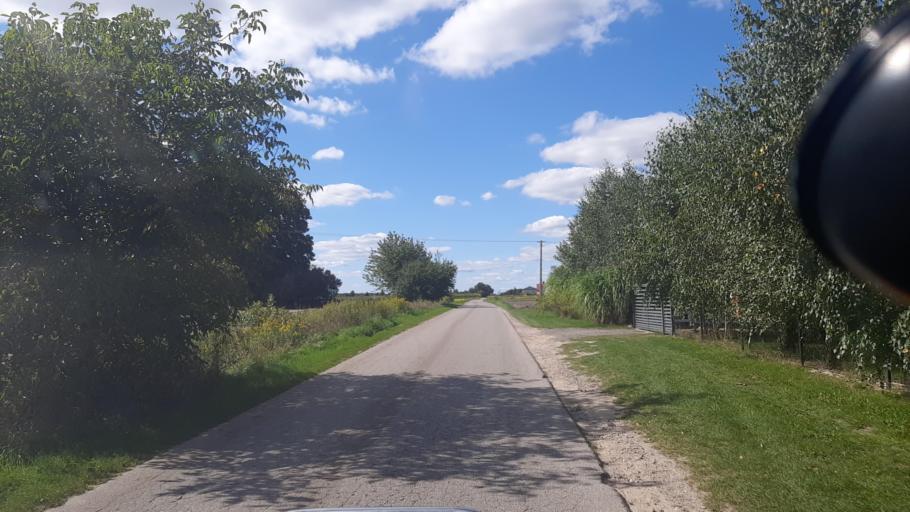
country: PL
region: Lublin Voivodeship
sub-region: Powiat lubartowski
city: Kamionka
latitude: 51.4045
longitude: 22.4095
